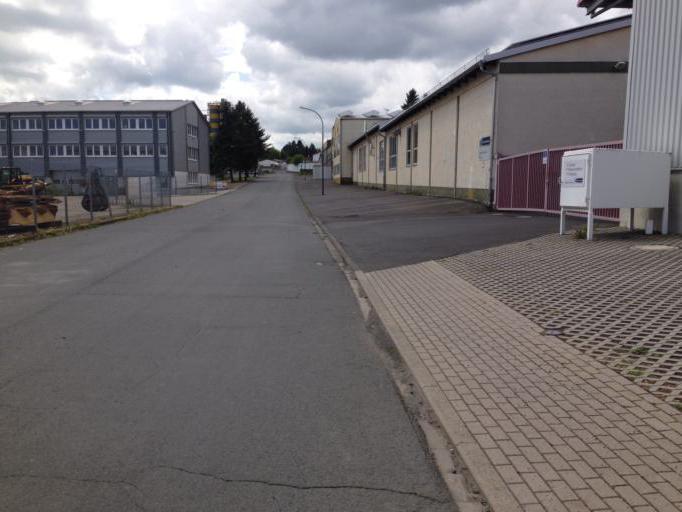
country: DE
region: Hesse
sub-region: Regierungsbezirk Giessen
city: Alsfeld
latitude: 50.7402
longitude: 9.2561
